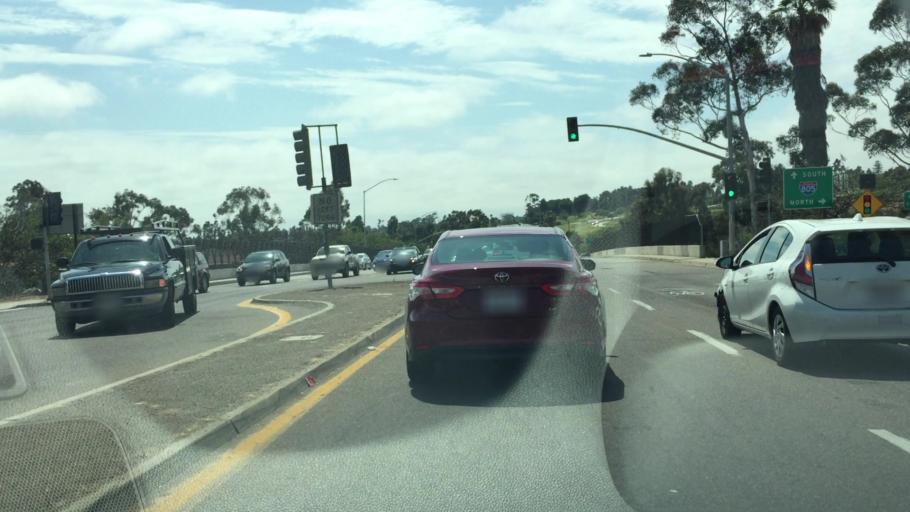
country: US
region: California
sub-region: San Diego County
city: National City
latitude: 32.7042
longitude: -117.0940
